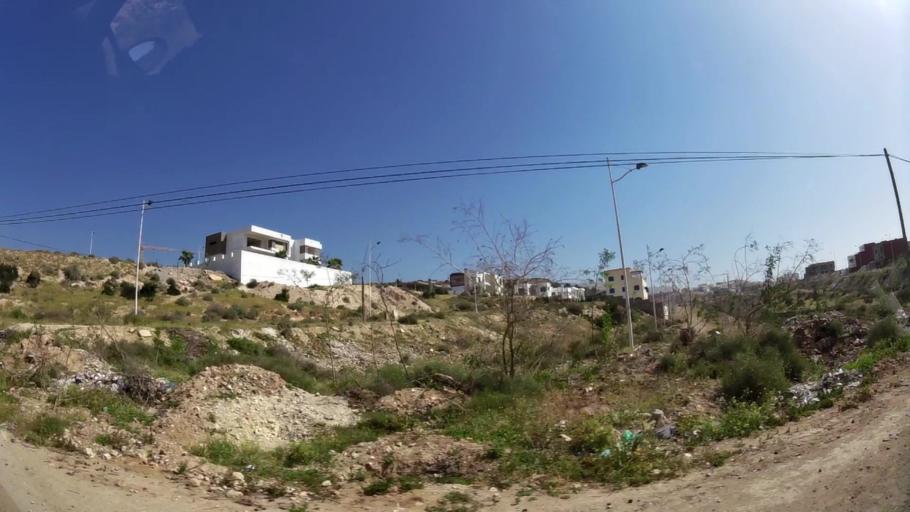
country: MA
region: Souss-Massa-Draa
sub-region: Agadir-Ida-ou-Tnan
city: Agadir
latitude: 30.4417
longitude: -9.5768
